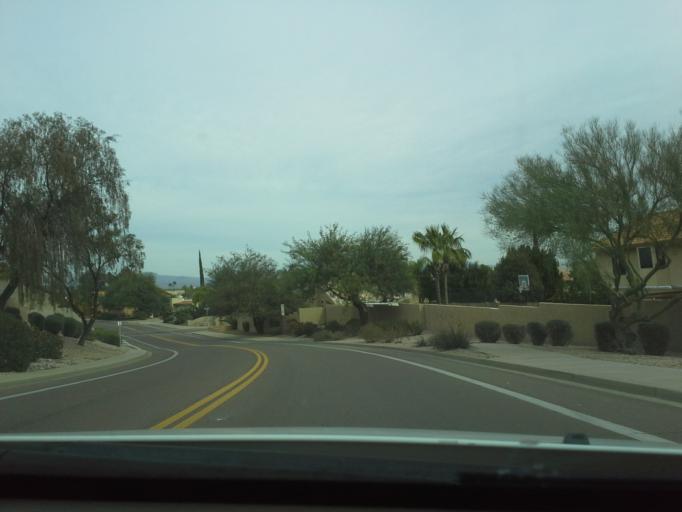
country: US
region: Arizona
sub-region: Maricopa County
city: Paradise Valley
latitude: 33.6144
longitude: -112.0206
